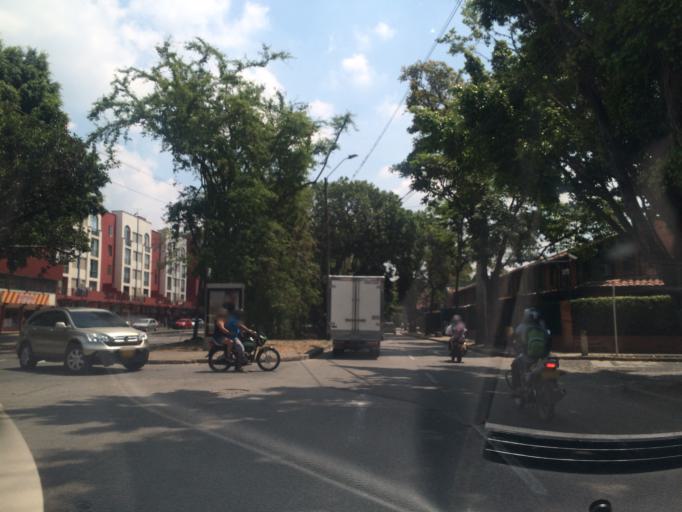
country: CO
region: Valle del Cauca
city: Cali
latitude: 3.4120
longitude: -76.5556
